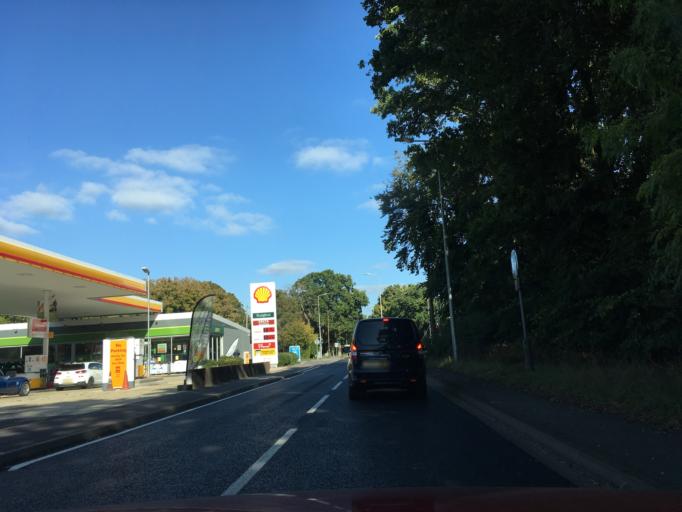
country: GB
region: England
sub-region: Hampshire
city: Tadley
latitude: 51.3602
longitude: -1.1490
